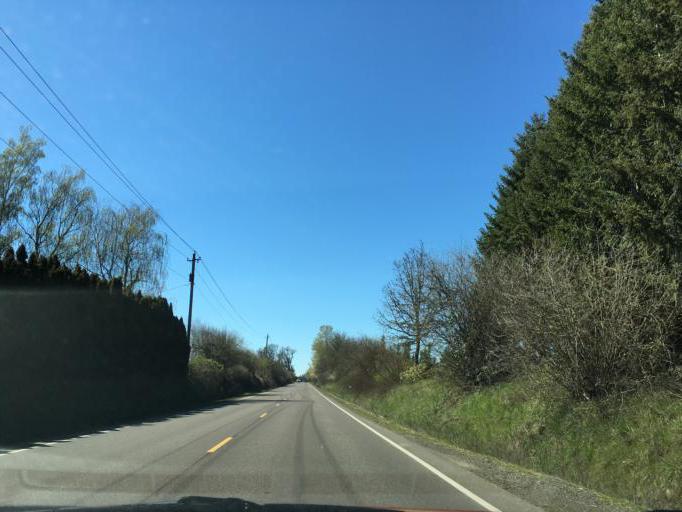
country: US
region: Oregon
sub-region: Marion County
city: Hubbard
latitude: 45.1443
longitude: -122.7457
